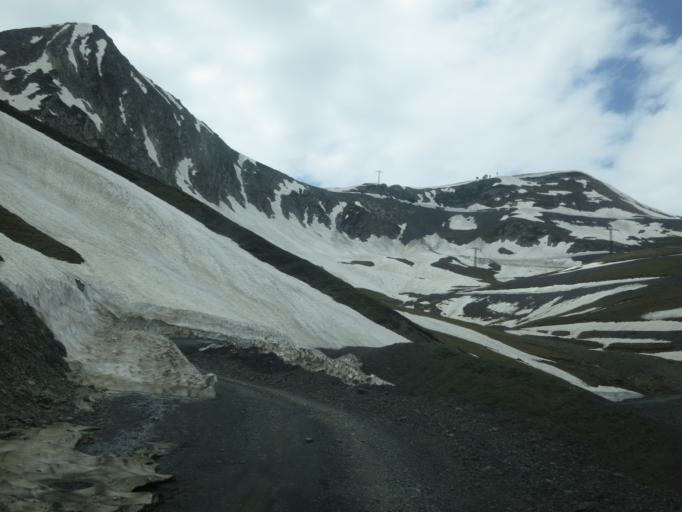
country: GE
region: Kakheti
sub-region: Telavi
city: Telavi
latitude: 42.2862
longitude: 45.5124
